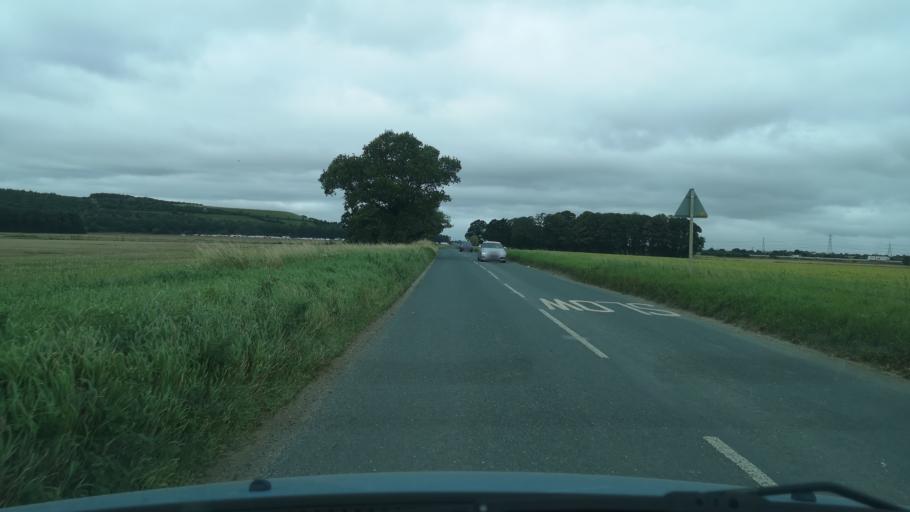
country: GB
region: England
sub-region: Doncaster
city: Norton
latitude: 53.6892
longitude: -1.1627
